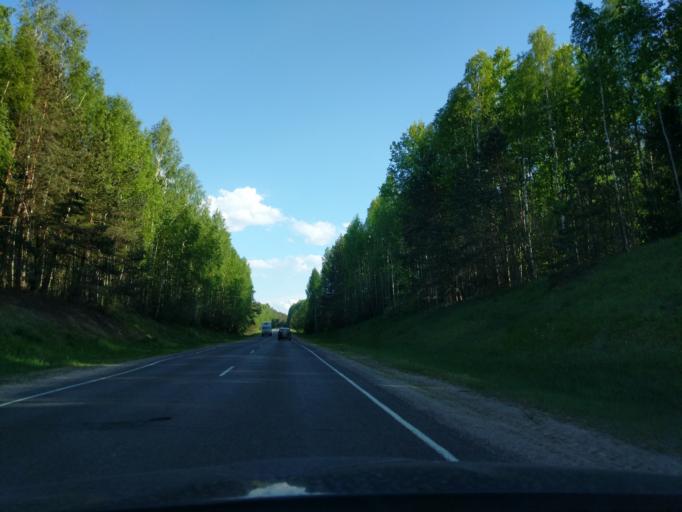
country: BY
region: Minsk
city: Kryvichy
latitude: 54.6024
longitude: 27.1849
